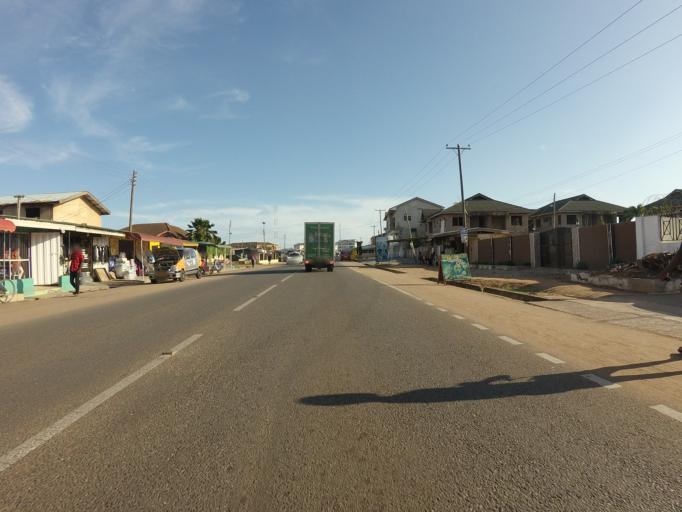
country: GH
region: Greater Accra
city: Nungua
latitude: 5.6322
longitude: -0.0900
